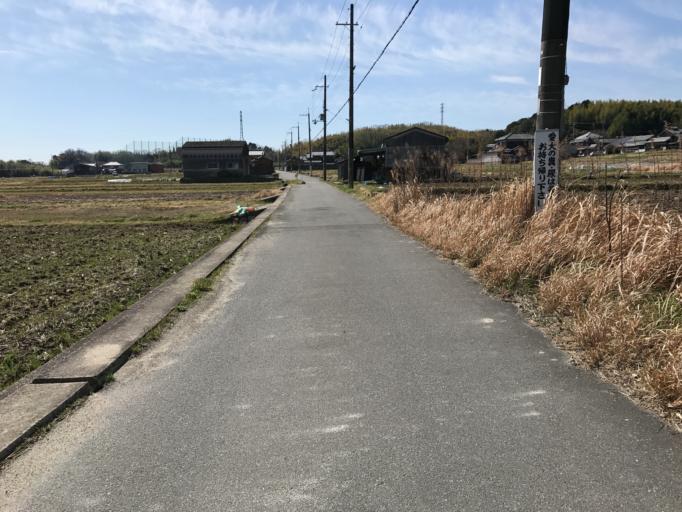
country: JP
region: Kyoto
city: Tanabe
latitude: 34.7885
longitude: 135.7831
